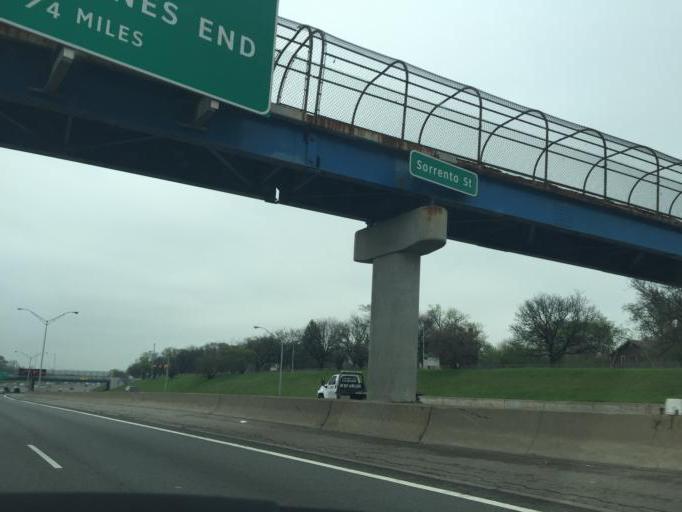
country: US
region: Michigan
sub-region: Wayne County
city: Dearborn
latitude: 42.3846
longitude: -83.1718
